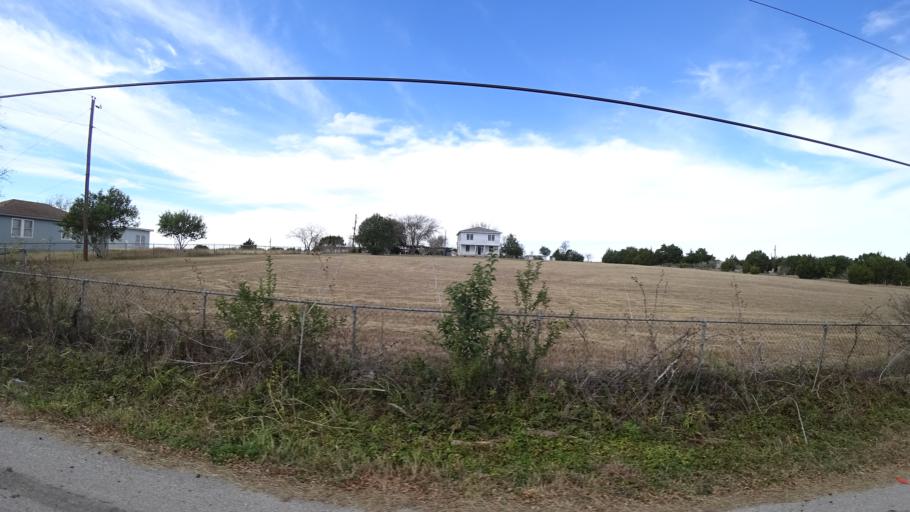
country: US
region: Texas
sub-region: Travis County
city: Onion Creek
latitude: 30.1234
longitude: -97.7329
